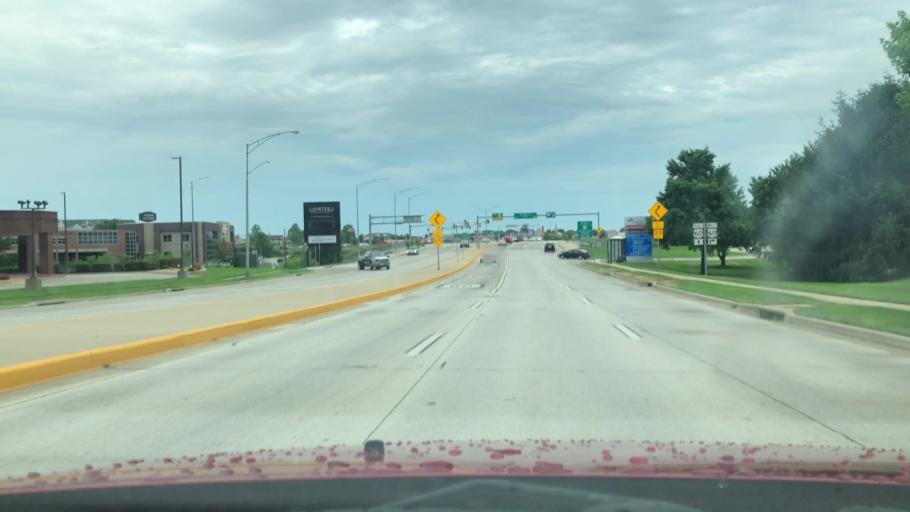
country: US
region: Missouri
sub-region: Greene County
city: Springfield
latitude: 37.1454
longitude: -93.2781
